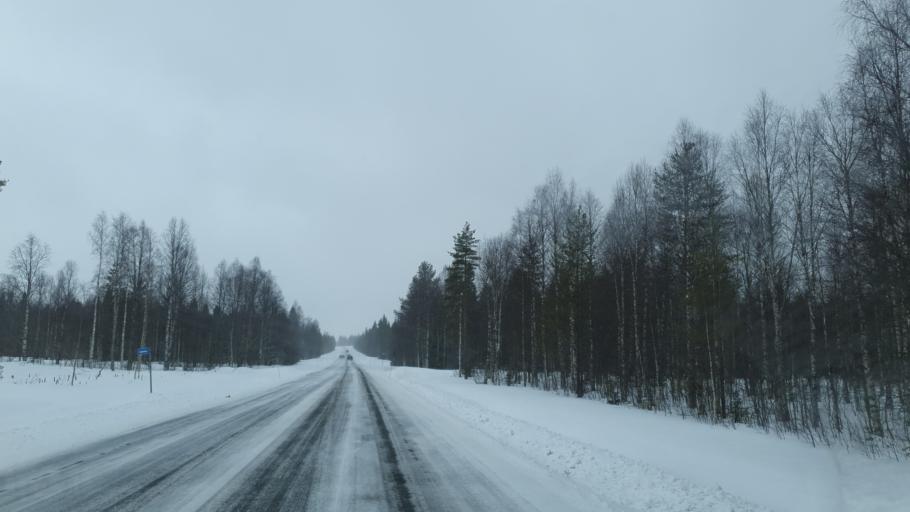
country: FI
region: Lapland
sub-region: Rovaniemi
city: Ranua
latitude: 66.0456
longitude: 26.3493
